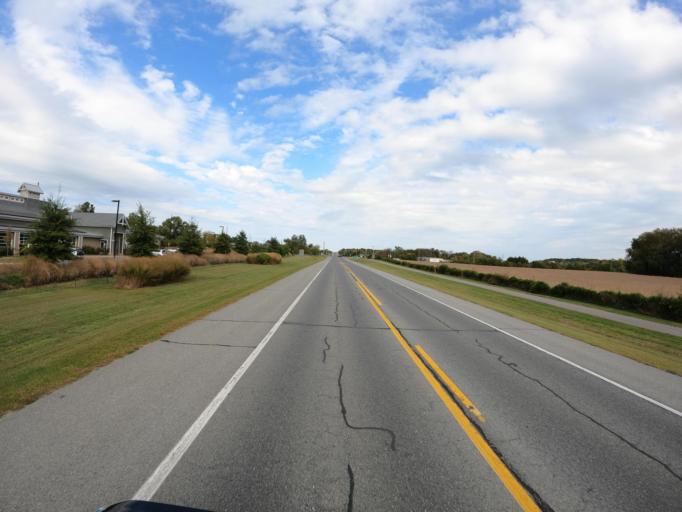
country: US
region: Delaware
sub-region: Sussex County
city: Lewes
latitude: 38.7660
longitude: -75.1407
